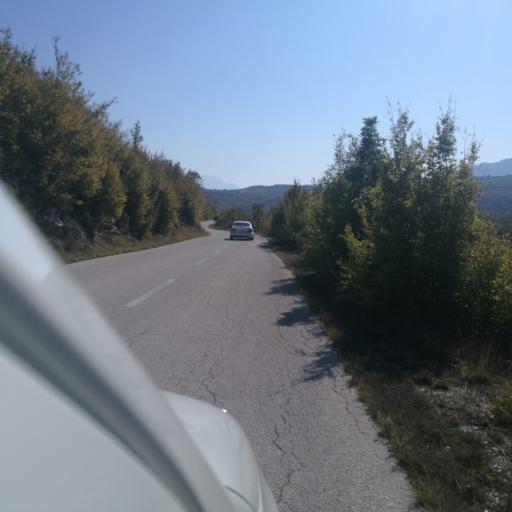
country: HR
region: Splitsko-Dalmatinska
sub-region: Grad Omis
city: Omis
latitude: 43.5212
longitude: 16.7525
